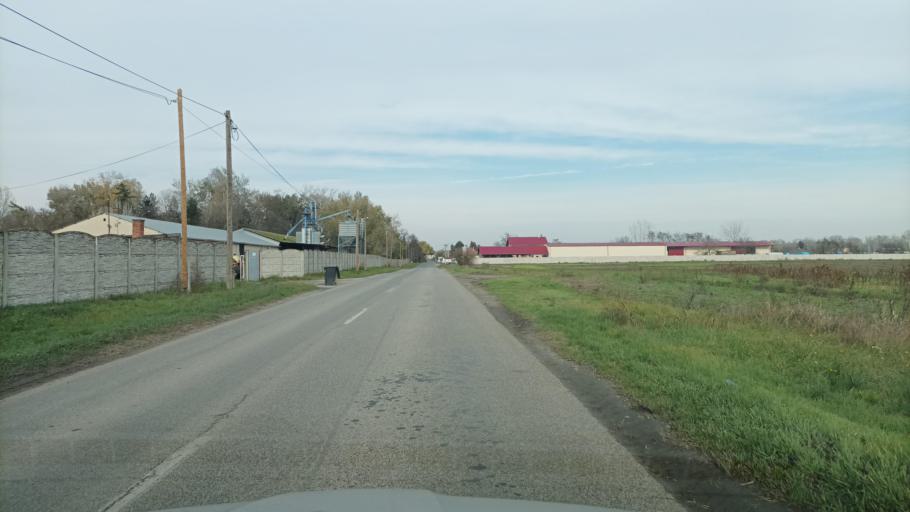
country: HU
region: Pest
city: Rackeve
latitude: 47.1210
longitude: 18.9463
